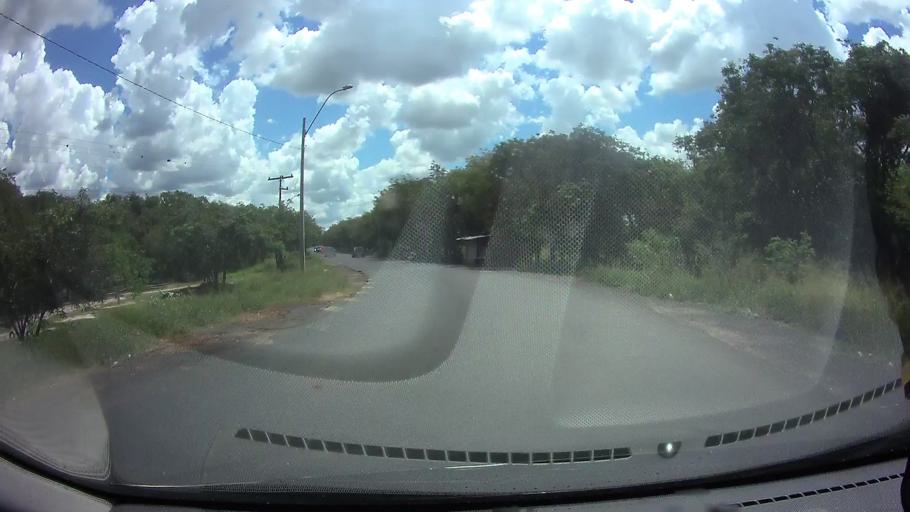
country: PY
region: Presidente Hayes
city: Nanawa
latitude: -25.2435
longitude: -57.6781
